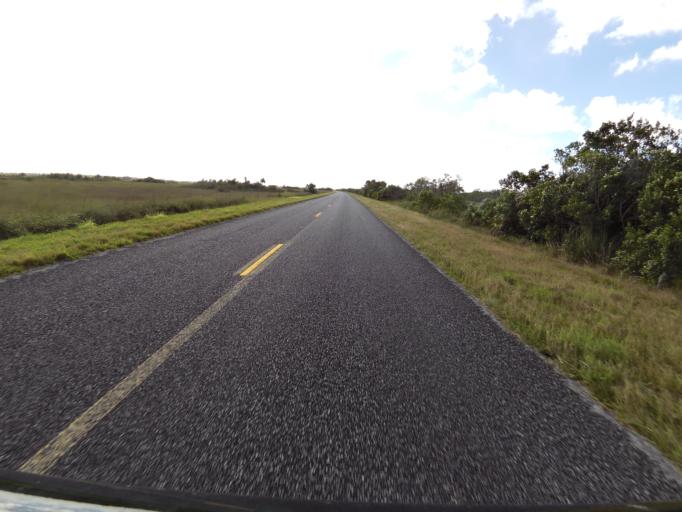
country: US
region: Florida
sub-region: Miami-Dade County
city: Florida City
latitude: 25.3917
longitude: -80.8018
